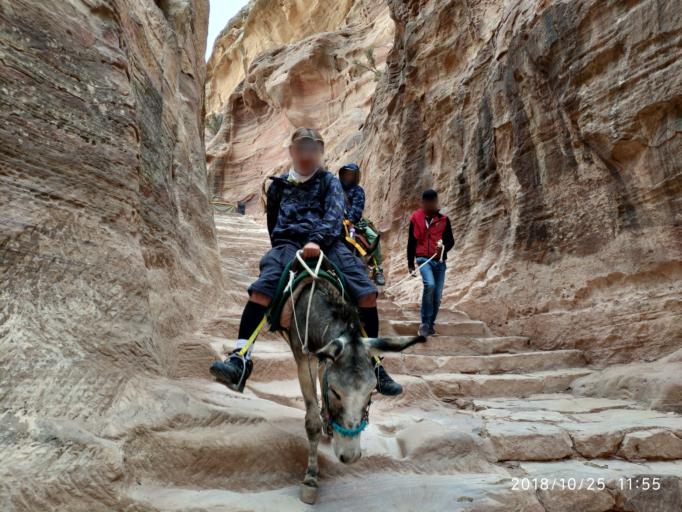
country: JO
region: Ma'an
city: Petra
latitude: 30.3363
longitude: 35.4343
